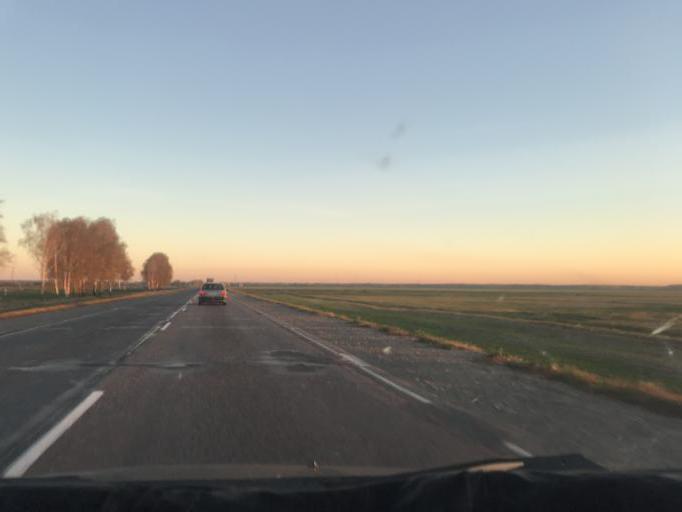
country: BY
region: Gomel
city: Kalinkavichy
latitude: 52.1525
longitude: 29.2449
